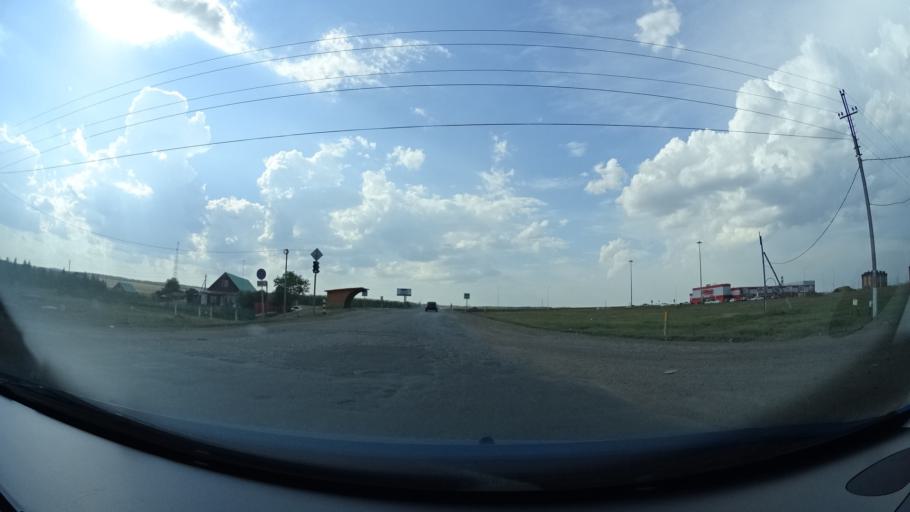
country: RU
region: Bashkortostan
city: Meleuz
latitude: 52.9643
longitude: 55.9103
